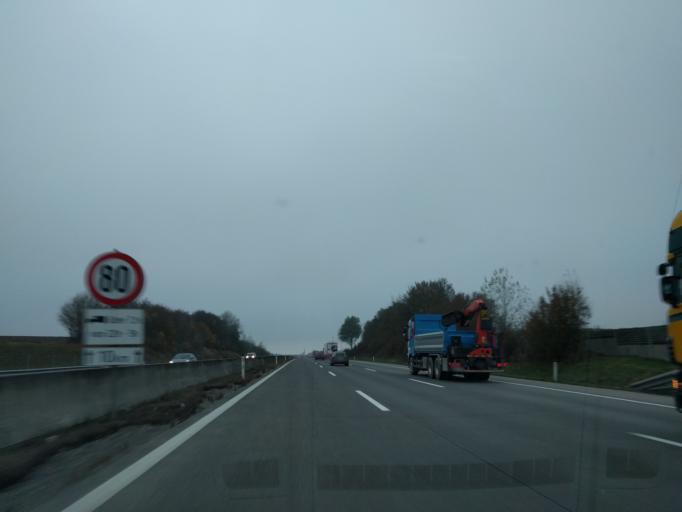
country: AT
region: Lower Austria
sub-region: Politischer Bezirk Sankt Polten
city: Sankt Margarethen an der Sierning
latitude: 48.1749
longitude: 15.4666
